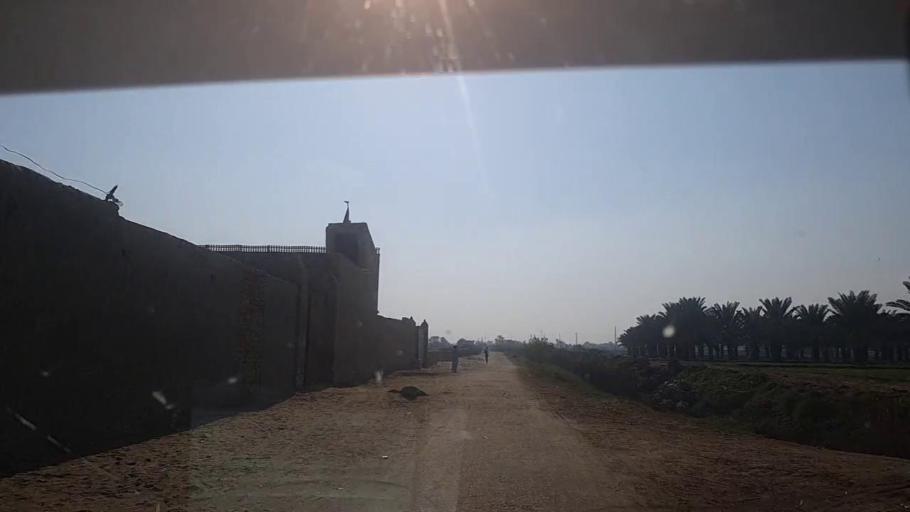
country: PK
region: Sindh
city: Gambat
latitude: 27.3650
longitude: 68.5587
